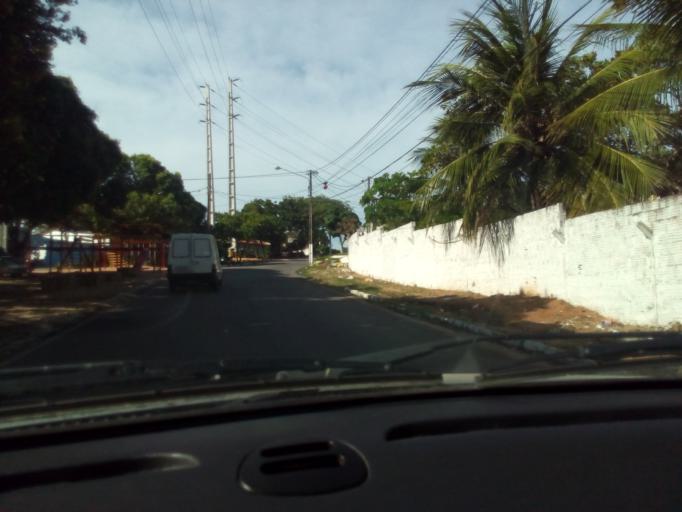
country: BR
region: Rio Grande do Norte
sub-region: Parnamirim
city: Parnamirim
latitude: -5.8746
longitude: -35.2094
